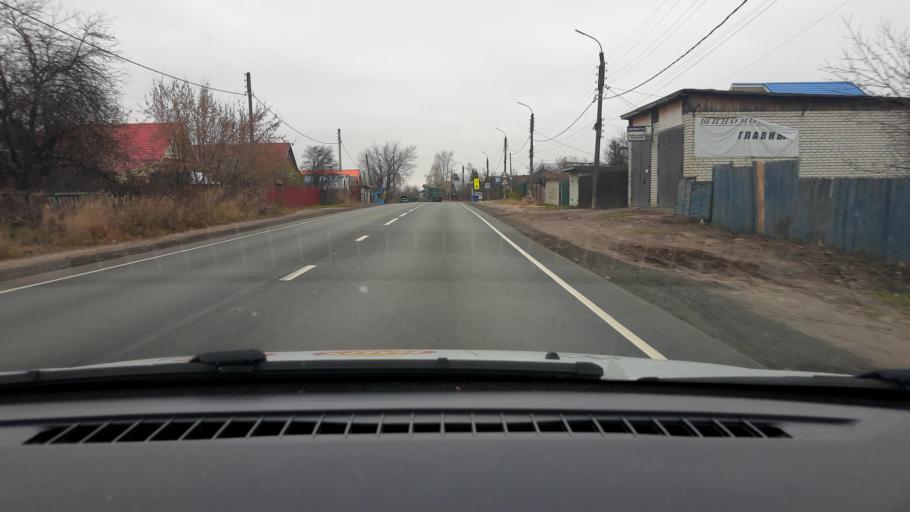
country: RU
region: Nizjnij Novgorod
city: Gidrotorf
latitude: 56.5367
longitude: 43.5375
